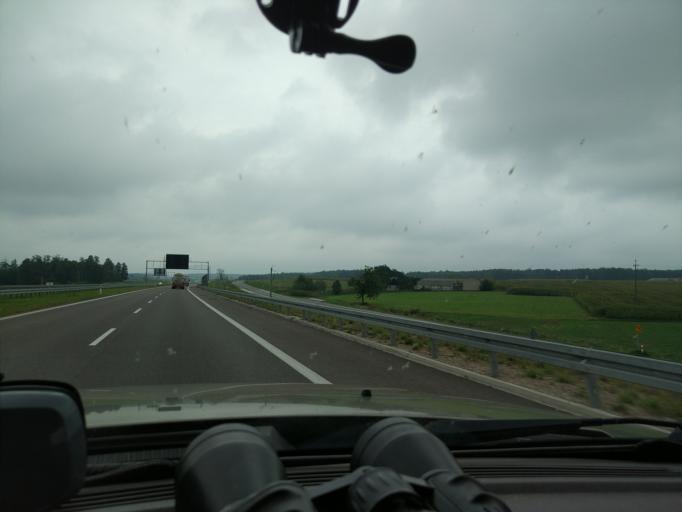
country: PL
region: Podlasie
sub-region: Powiat zambrowski
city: Rutki-Kossaki
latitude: 53.0479
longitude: 22.3743
